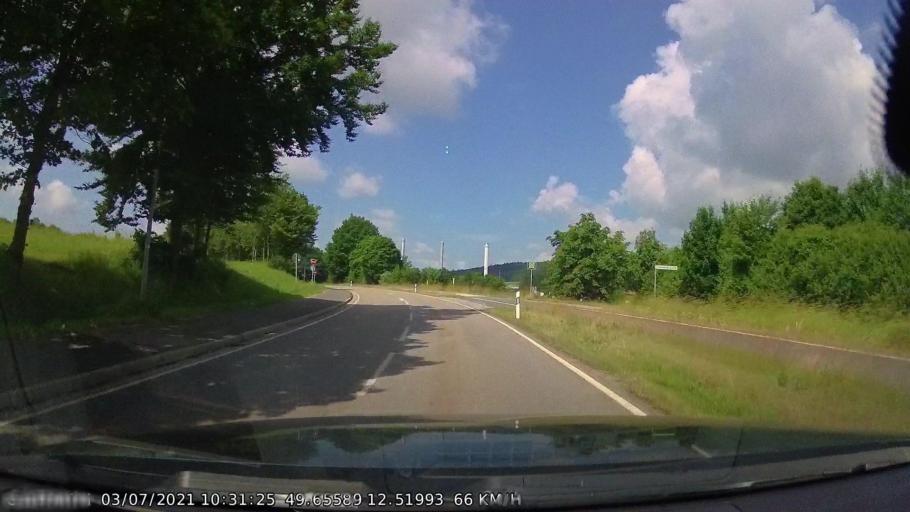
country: DE
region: Bavaria
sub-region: Upper Palatinate
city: Waidhaus
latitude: 49.6559
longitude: 12.5198
